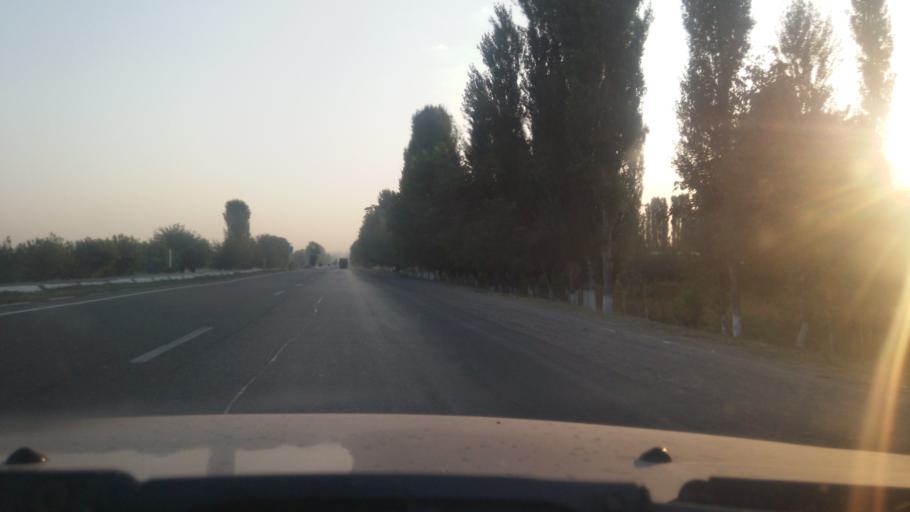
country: UZ
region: Toshkent
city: Urtaowul
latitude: 41.1778
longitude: 69.0755
